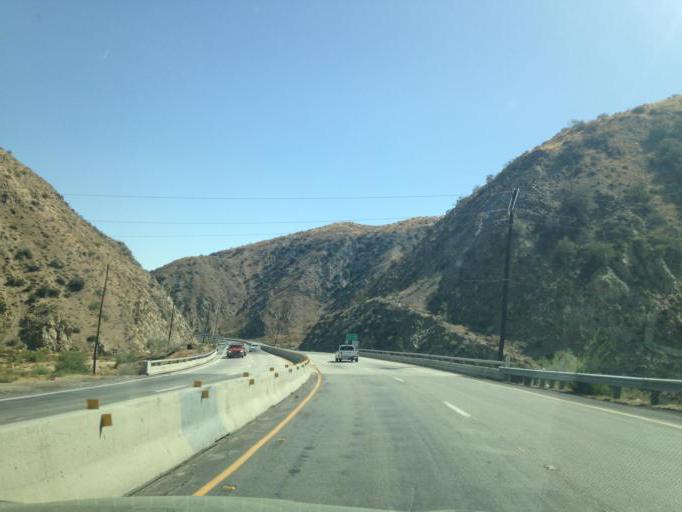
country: US
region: California
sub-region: San Bernardino County
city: Morongo Valley
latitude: 34.0335
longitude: -116.5919
